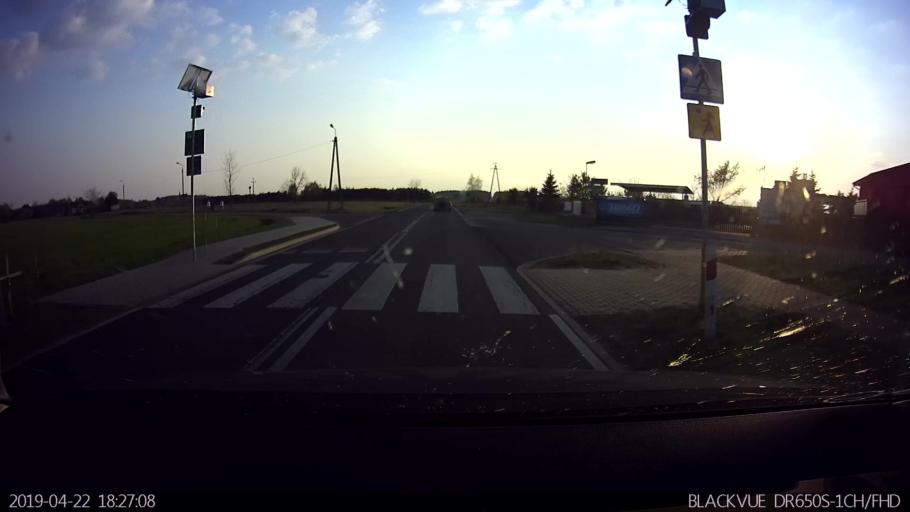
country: PL
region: Masovian Voivodeship
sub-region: Powiat wolominski
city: Tluszcz
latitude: 52.4667
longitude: 21.5020
